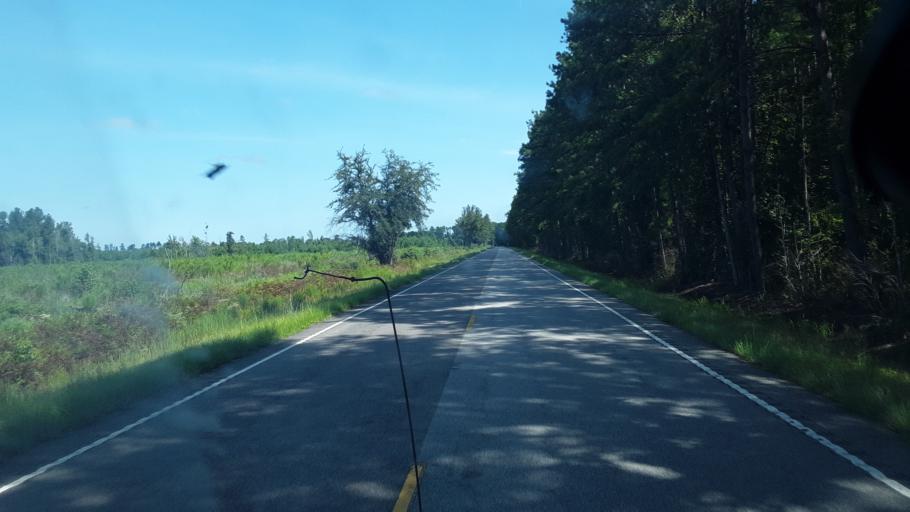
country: US
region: South Carolina
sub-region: Hampton County
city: Varnville
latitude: 32.8215
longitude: -81.0516
